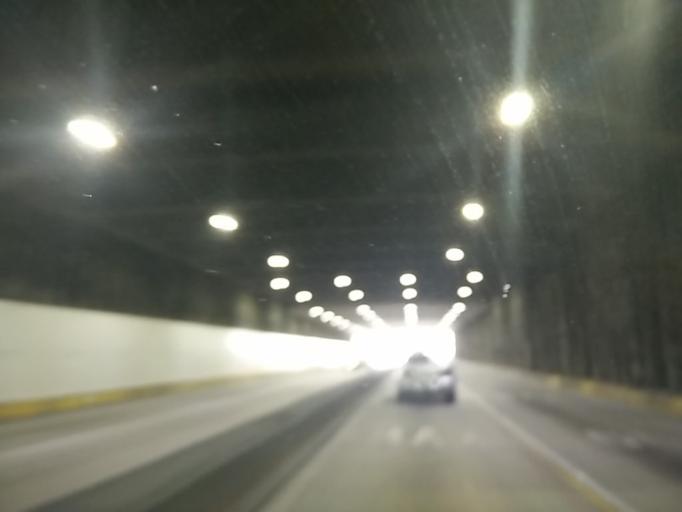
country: MX
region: Jalisco
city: Guadalajara
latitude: 20.6709
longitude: -103.4046
